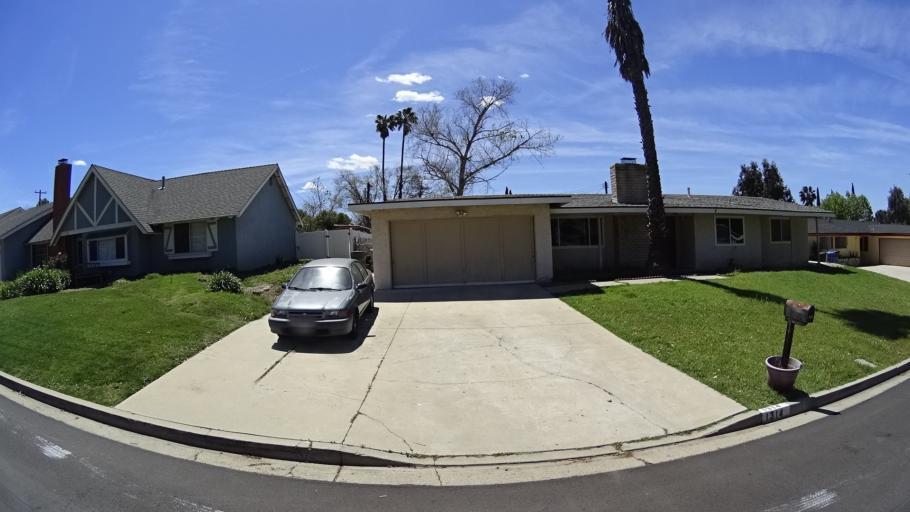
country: US
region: California
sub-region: Ventura County
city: Thousand Oaks
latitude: 34.2166
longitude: -118.8559
